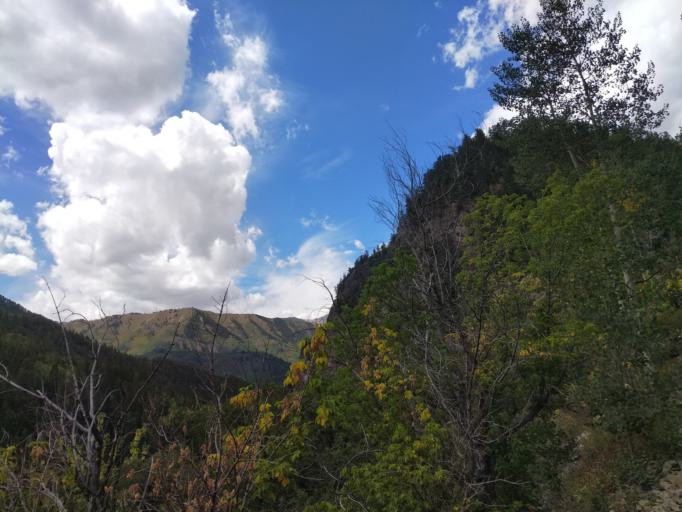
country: US
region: Colorado
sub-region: Pitkin County
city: Snowmass Village
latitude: 39.0695
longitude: -107.1525
